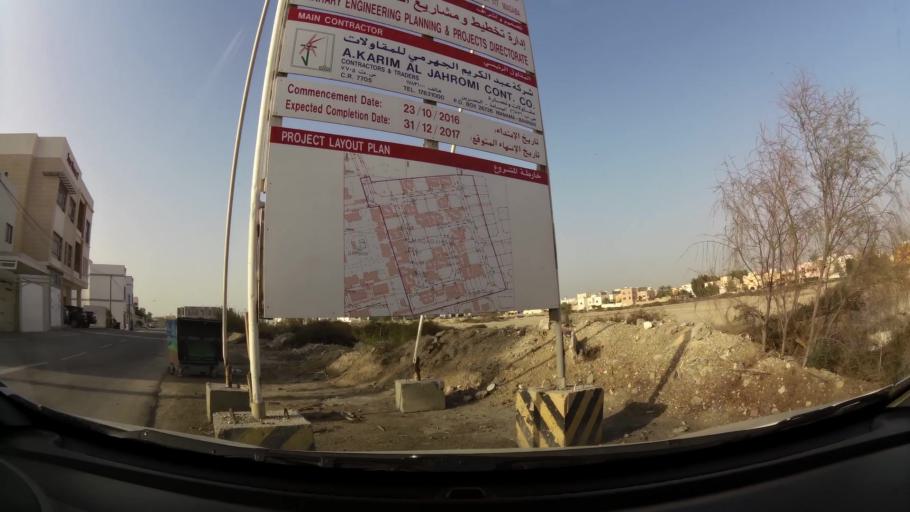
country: BH
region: Manama
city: Jidd Hafs
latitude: 26.2035
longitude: 50.4896
